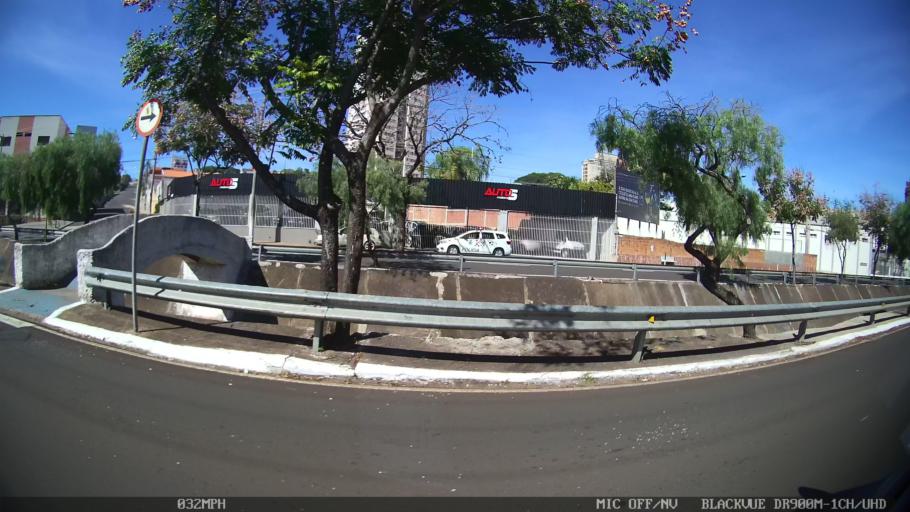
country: BR
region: Sao Paulo
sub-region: Franca
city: Franca
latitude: -20.5402
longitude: -47.3944
